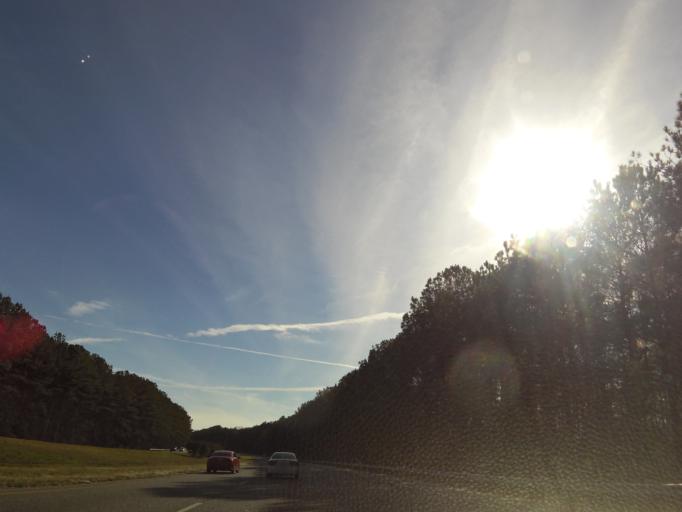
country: US
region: Georgia
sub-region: Harris County
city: Hamilton
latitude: 32.7426
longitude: -85.0192
